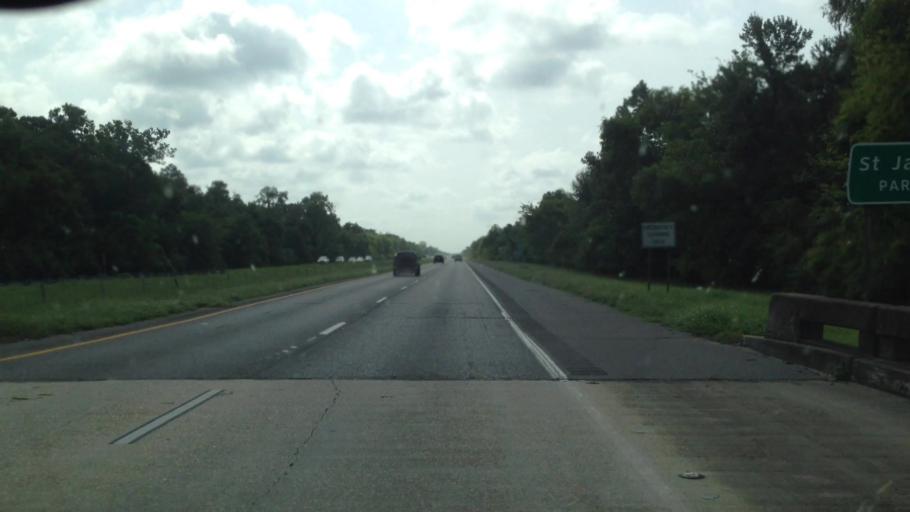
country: US
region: Louisiana
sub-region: Saint James Parish
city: Grand Point
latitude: 30.1439
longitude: -90.7606
